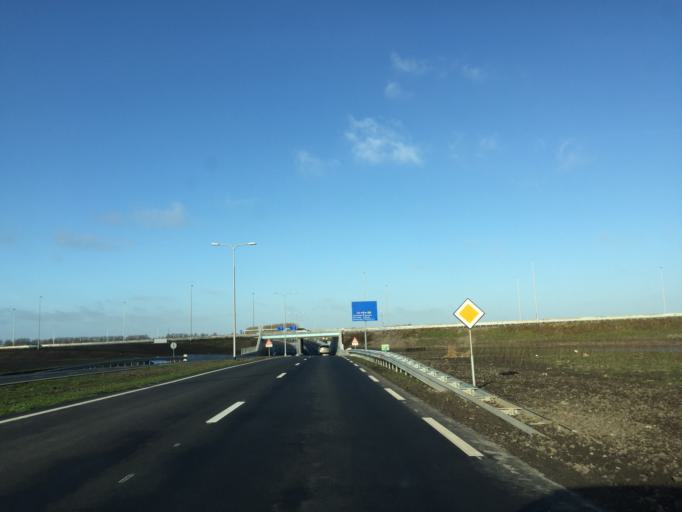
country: NL
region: South Holland
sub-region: Gemeente Waddinxveen
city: Waddinxveen
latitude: 52.0189
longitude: 4.6439
